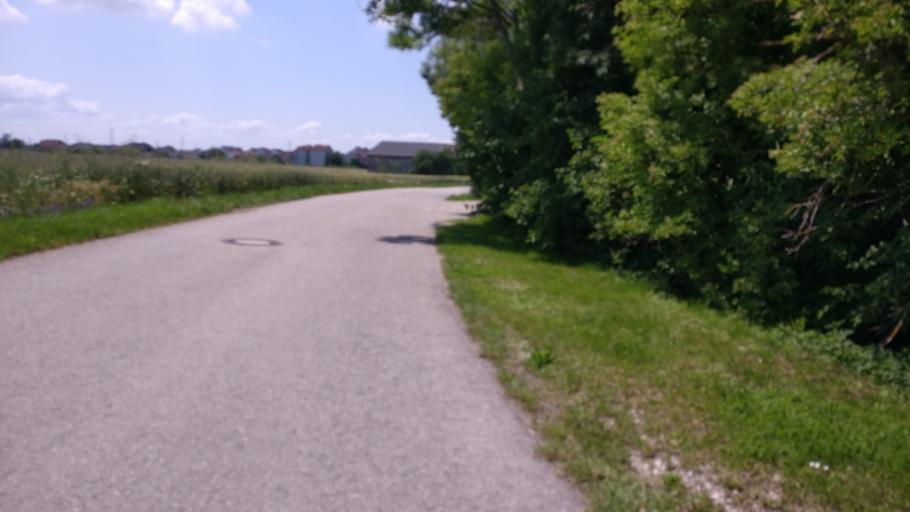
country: AT
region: Lower Austria
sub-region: Politischer Bezirk Baden
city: Schonau an der Triesting
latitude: 47.9368
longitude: 16.2587
